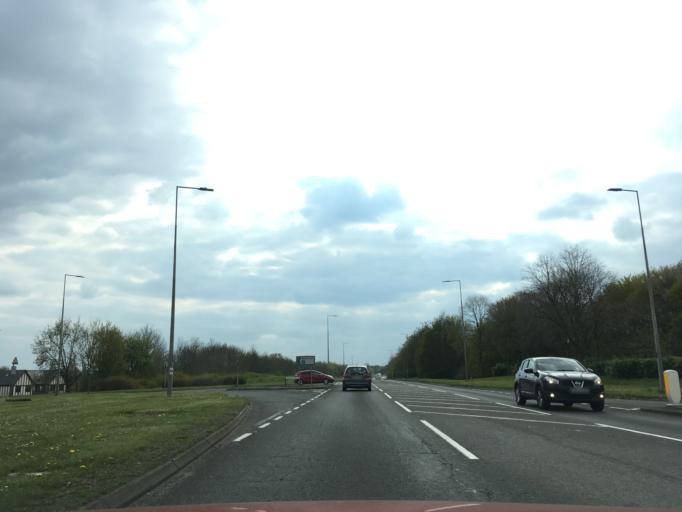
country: GB
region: England
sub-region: Milton Keynes
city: Loughton
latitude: 52.0173
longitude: -0.7700
